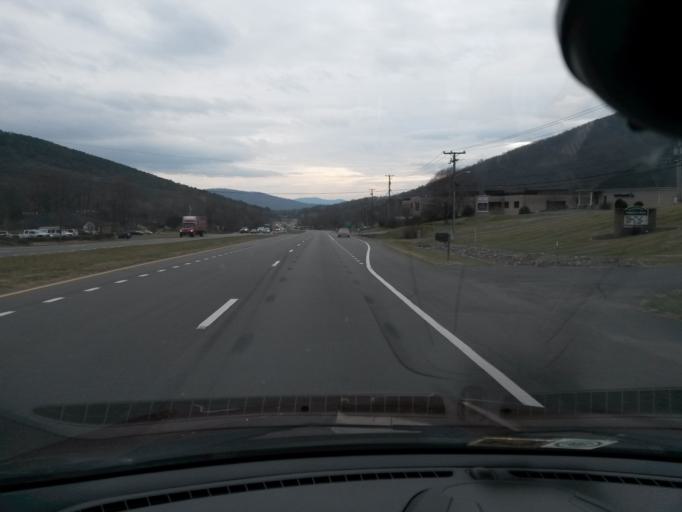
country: US
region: Virginia
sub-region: Botetourt County
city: Cloverdale
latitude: 37.3584
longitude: -79.8854
